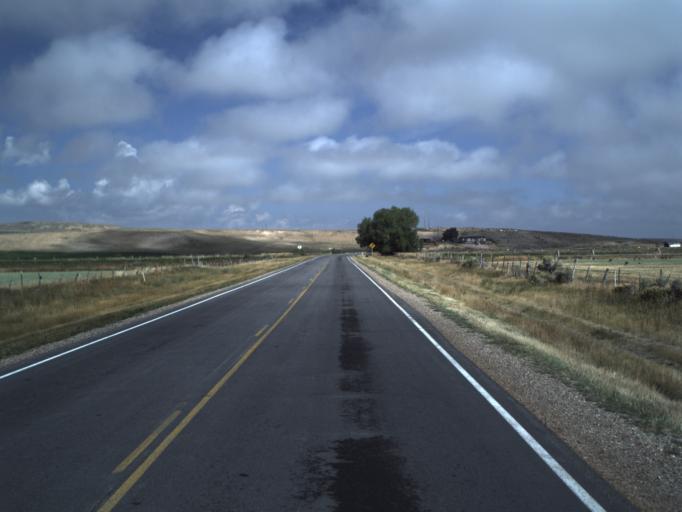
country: US
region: Utah
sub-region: Rich County
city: Randolph
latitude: 41.6732
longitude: -111.1850
